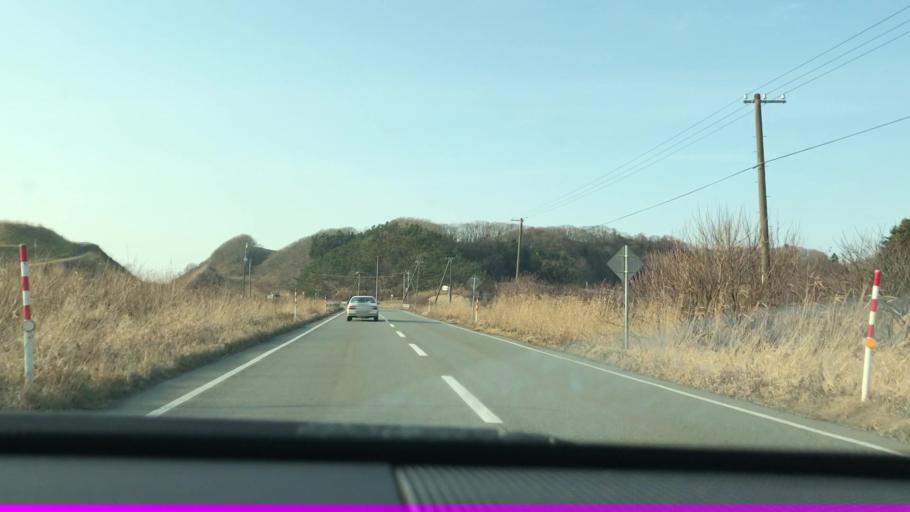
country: JP
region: Hokkaido
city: Shizunai-furukawacho
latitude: 42.2305
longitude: 142.6125
